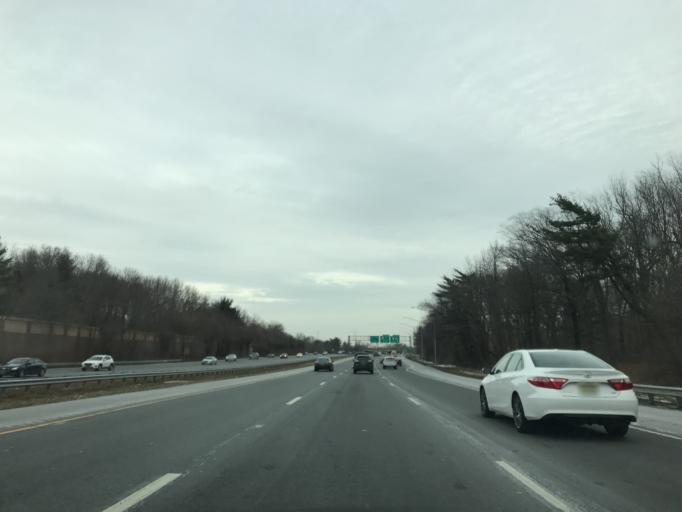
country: US
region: New Jersey
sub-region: Camden County
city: Kingston Estates
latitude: 39.9308
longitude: -74.9709
